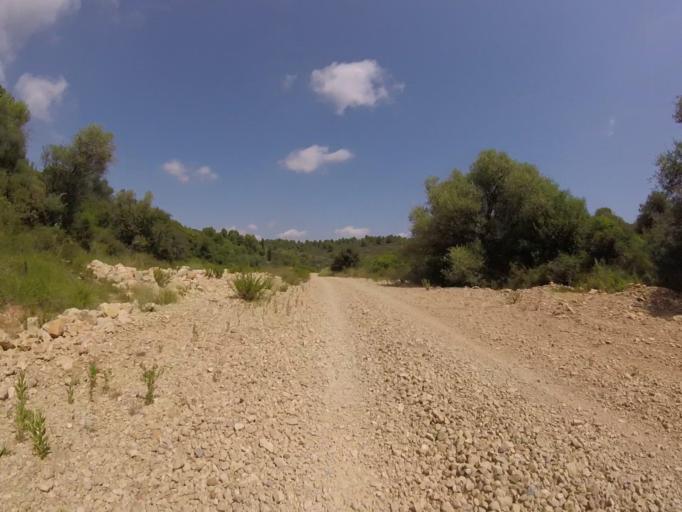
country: ES
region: Valencia
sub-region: Provincia de Castello
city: Torreblanca
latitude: 40.2110
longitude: 0.1395
